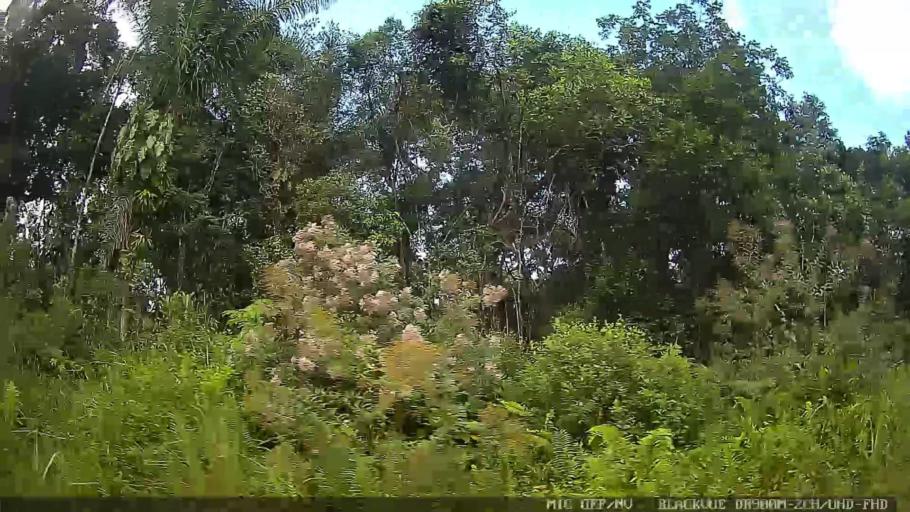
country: BR
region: Sao Paulo
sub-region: Itanhaem
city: Itanhaem
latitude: -24.1778
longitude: -46.9335
